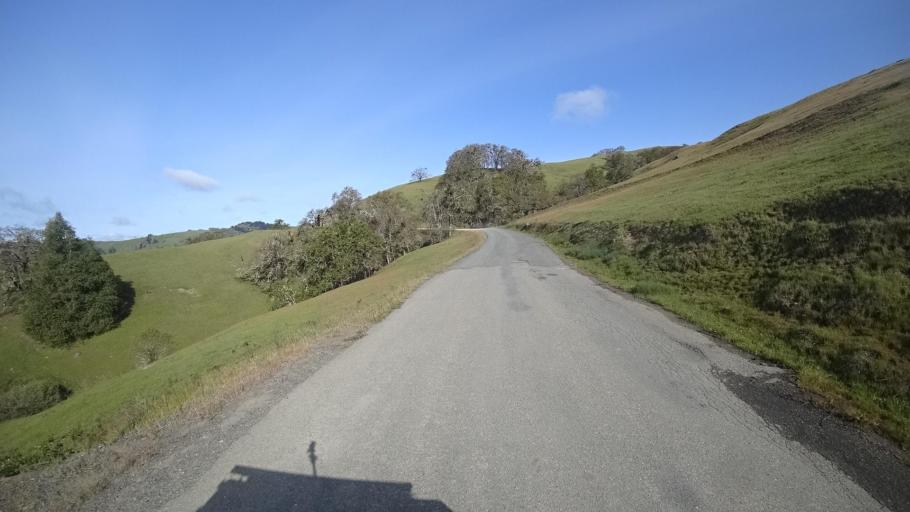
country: US
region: California
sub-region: Humboldt County
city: Hydesville
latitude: 40.6385
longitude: -123.8984
